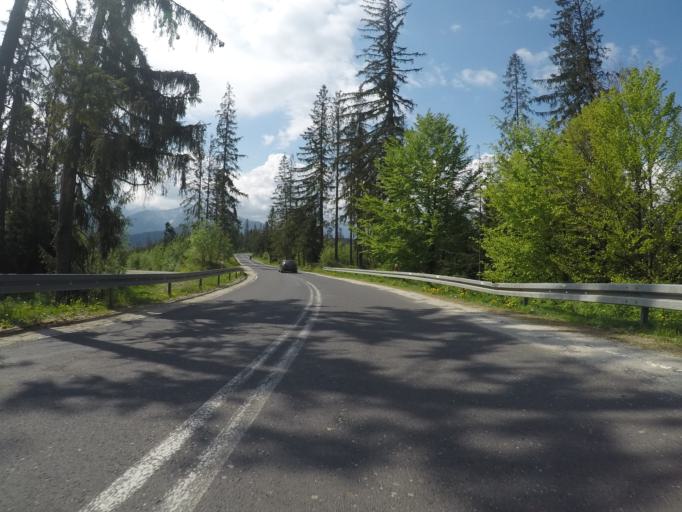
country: PL
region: Lesser Poland Voivodeship
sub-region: Powiat tatrzanski
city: Bukowina Tatrzanska
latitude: 49.2950
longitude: 20.1141
